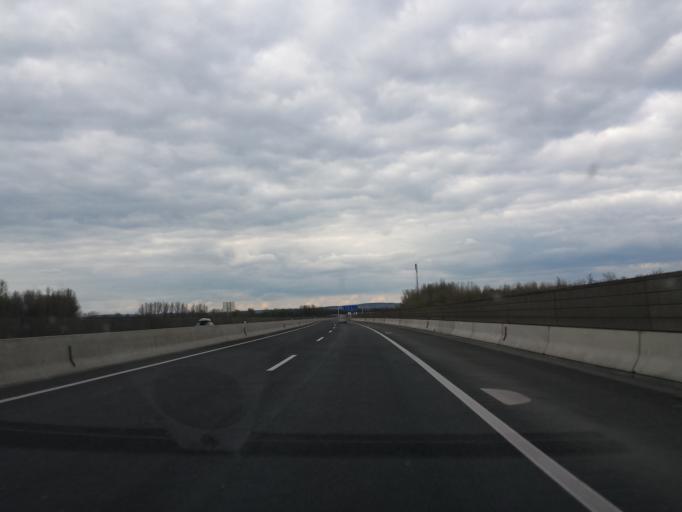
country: AT
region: Lower Austria
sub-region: Politischer Bezirk Krems
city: Grafenegg
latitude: 48.3943
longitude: 15.7322
